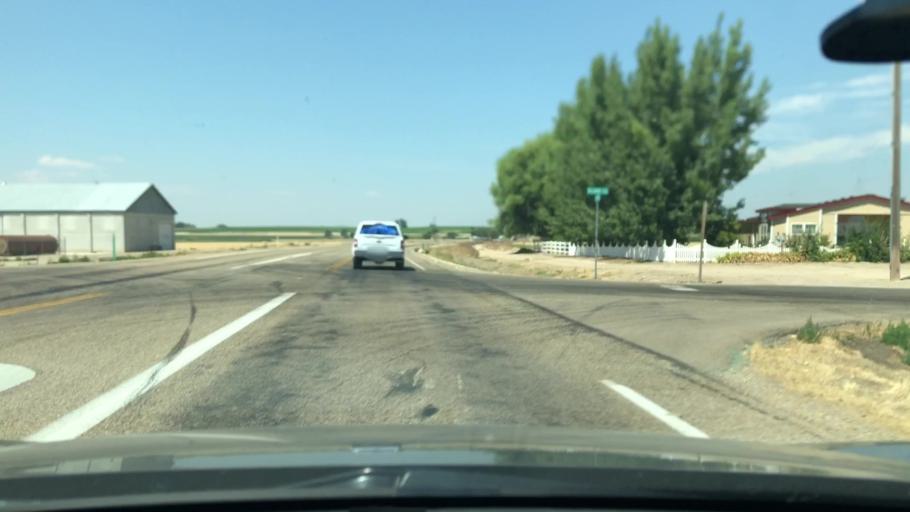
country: US
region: Idaho
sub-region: Canyon County
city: Parma
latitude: 43.8071
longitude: -116.9535
